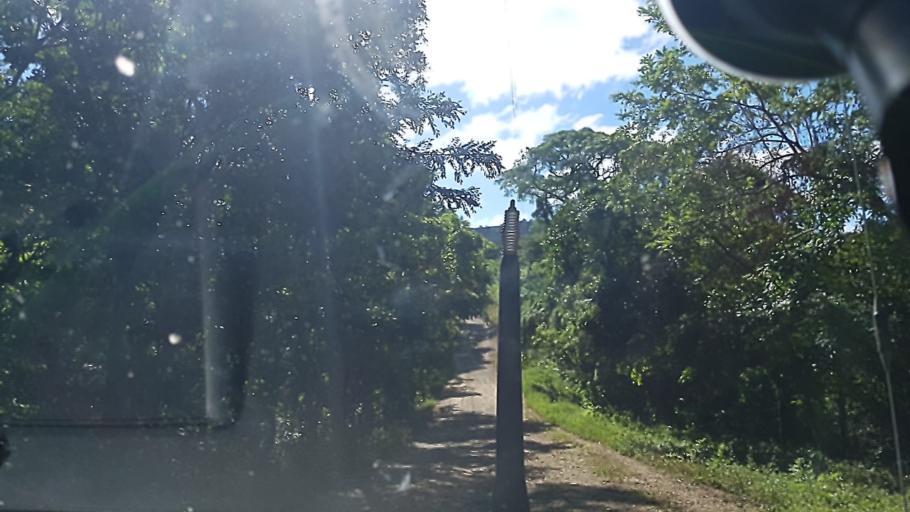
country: NI
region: Carazo
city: Santa Teresa
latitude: 11.6426
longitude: -86.1822
